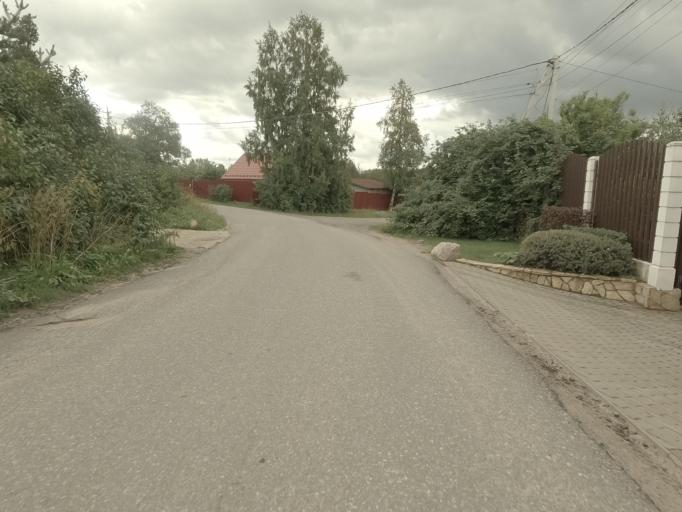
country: RU
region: Leningrad
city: Koltushi
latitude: 59.8907
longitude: 30.6883
